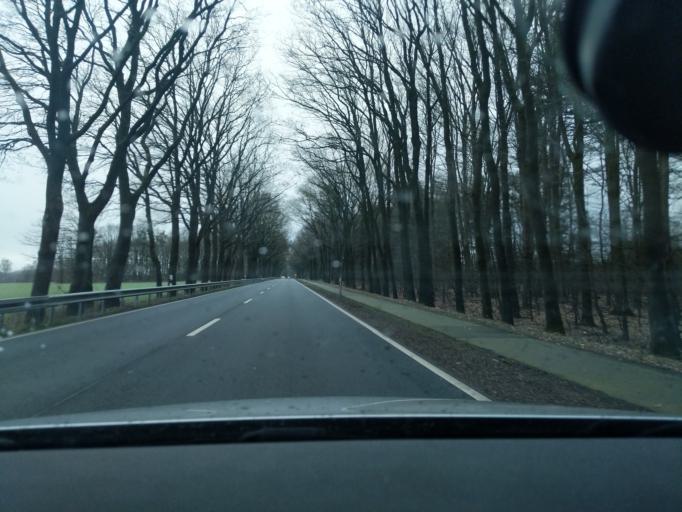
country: DE
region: Lower Saxony
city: Heinbockel
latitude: 53.5471
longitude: 9.3428
